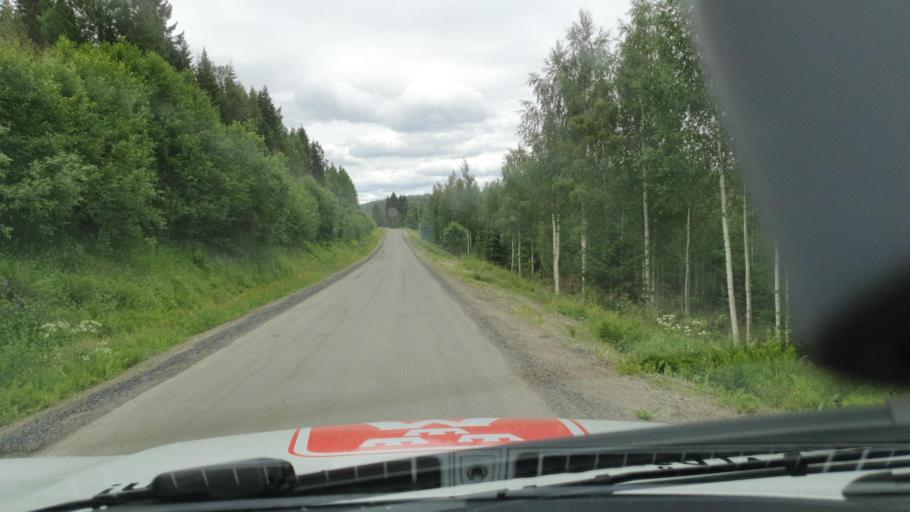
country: SE
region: Vaesterbotten
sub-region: Nordmalings Kommun
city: Nordmaling
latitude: 63.6590
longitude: 19.4428
